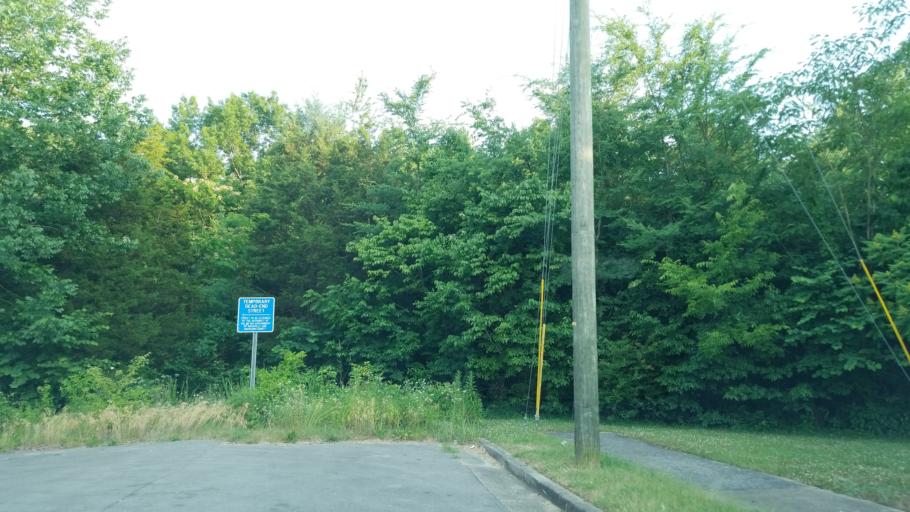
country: US
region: Tennessee
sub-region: Rutherford County
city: La Vergne
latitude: 36.0595
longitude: -86.5921
